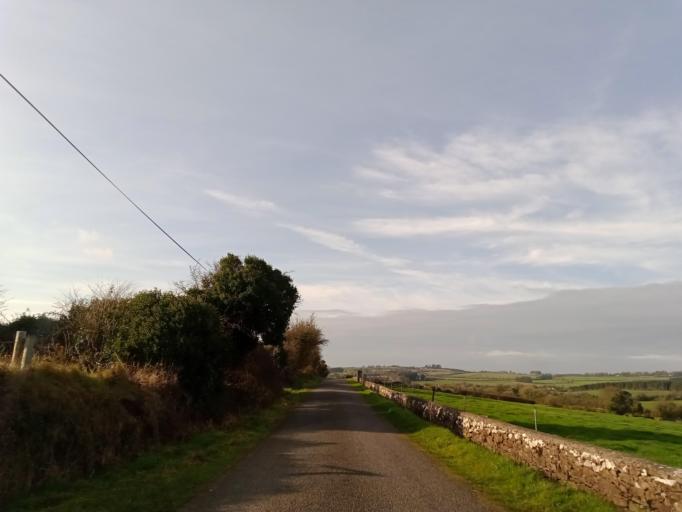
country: IE
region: Munster
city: Fethard
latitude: 52.5626
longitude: -7.6154
